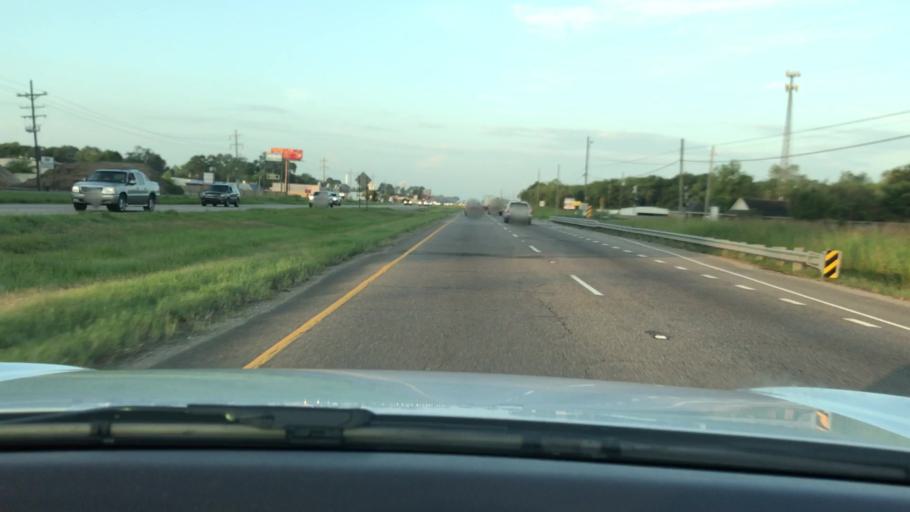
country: US
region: Louisiana
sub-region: West Baton Rouge Parish
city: Brusly
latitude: 30.4131
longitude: -91.2256
